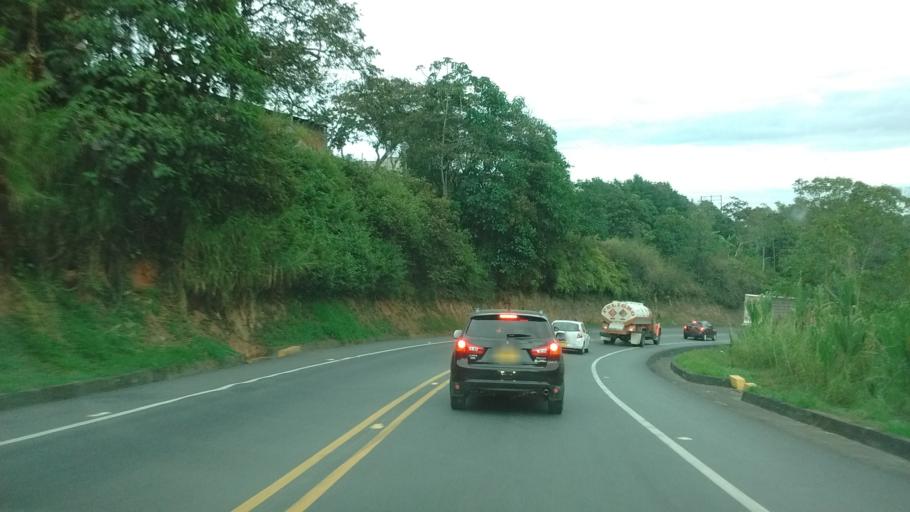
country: CO
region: Cauca
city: Caldono
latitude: 2.7885
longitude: -76.5520
